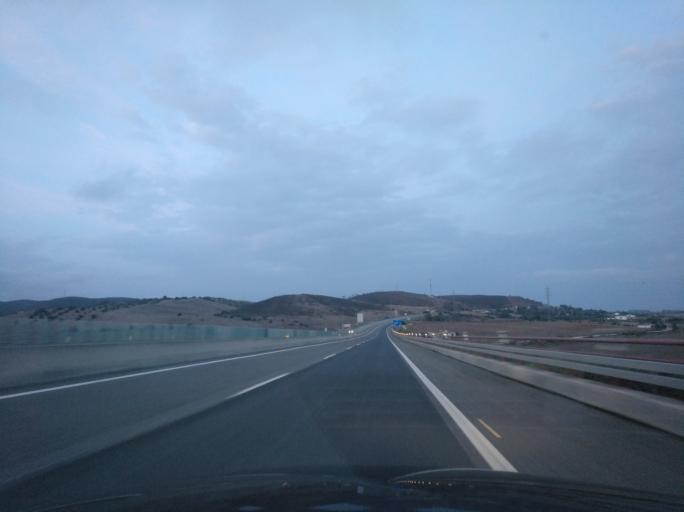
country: PT
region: Faro
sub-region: Lagos
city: Lagos
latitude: 37.1594
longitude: -8.6871
